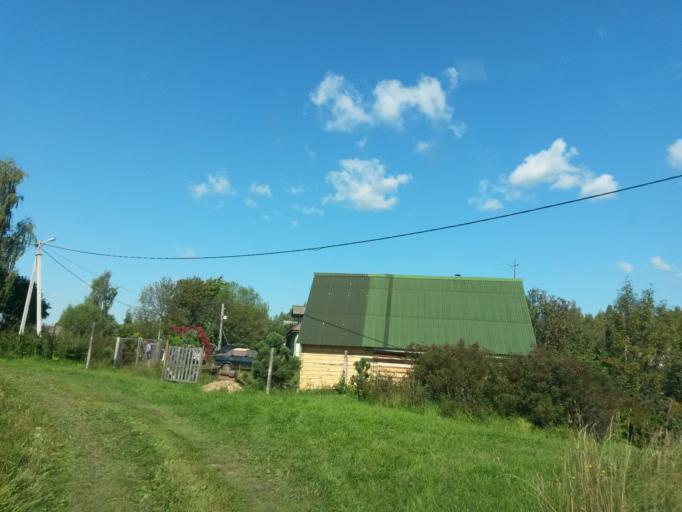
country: RU
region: Jaroslavl
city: Burmakino
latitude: 57.3861
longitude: 40.2136
